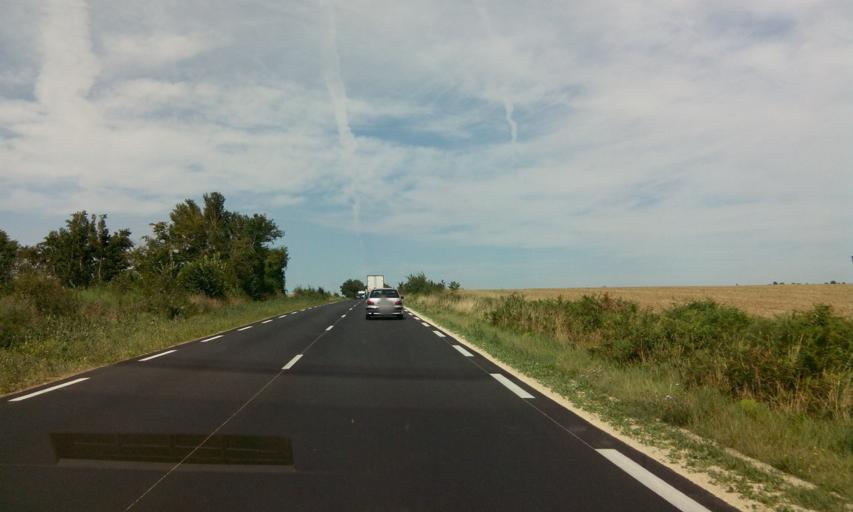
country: FR
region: Poitou-Charentes
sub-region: Departement des Deux-Sevres
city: Sauze-Vaussais
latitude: 46.1417
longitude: 0.0891
